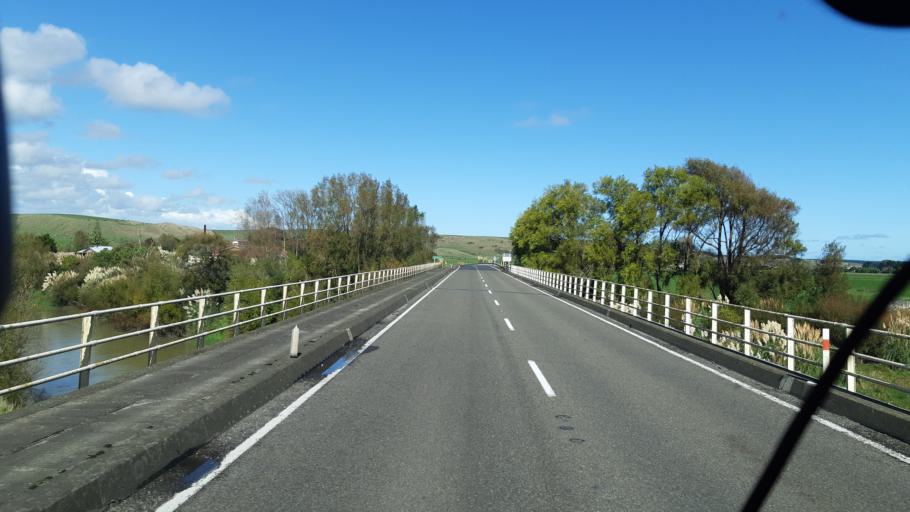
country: NZ
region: Manawatu-Wanganui
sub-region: Wanganui District
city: Wanganui
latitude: -40.0042
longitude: 175.1669
